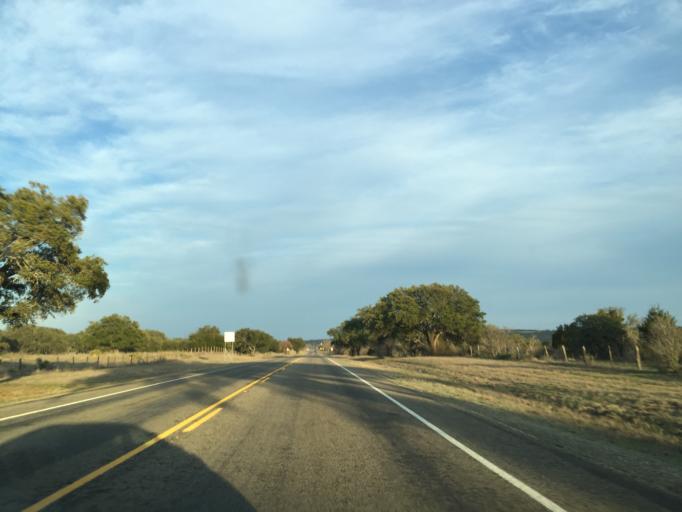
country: US
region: Texas
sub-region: Llano County
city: Buchanan Dam
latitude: 30.7330
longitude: -98.4786
